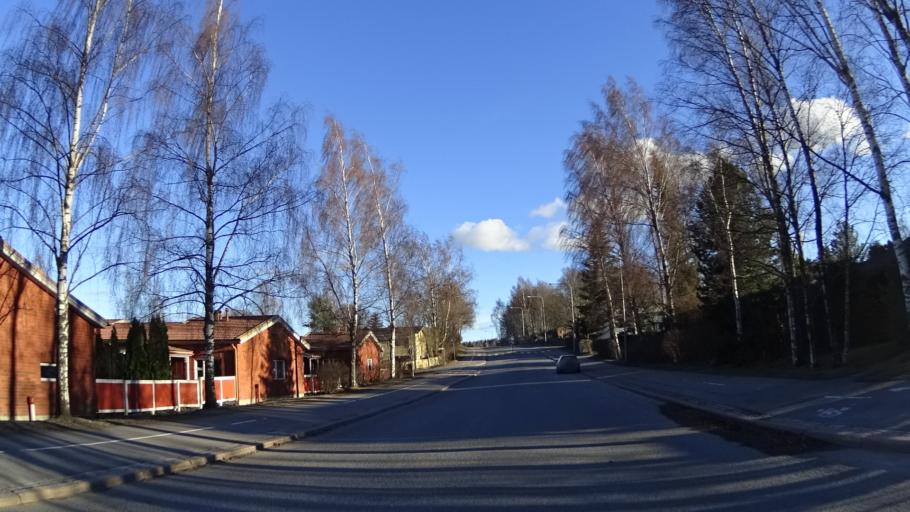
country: FI
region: Uusimaa
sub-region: Helsinki
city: Helsinki
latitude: 60.2474
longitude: 24.9581
